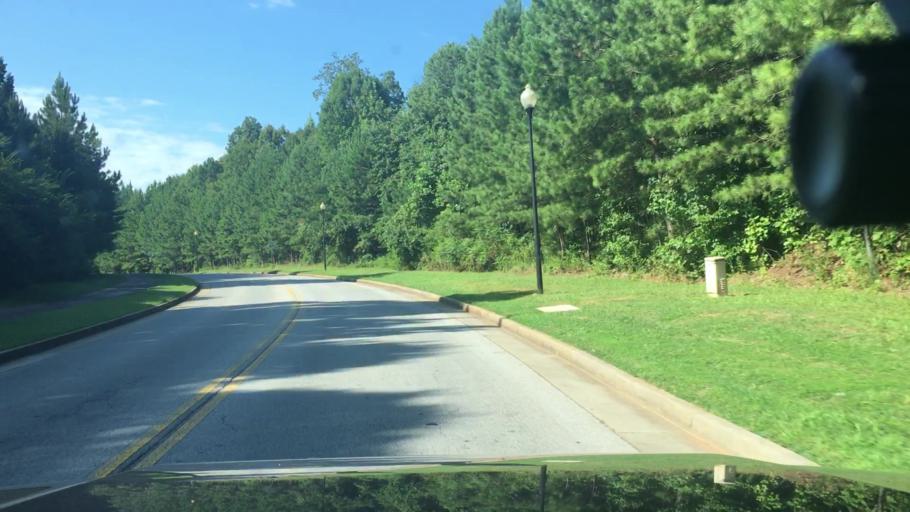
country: US
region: Georgia
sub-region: Coweta County
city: East Newnan
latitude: 33.3698
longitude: -84.7566
